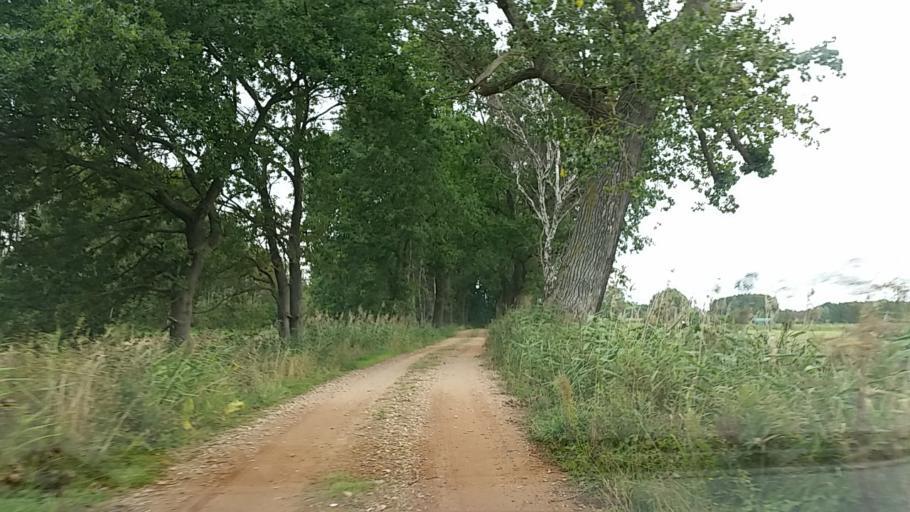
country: DE
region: Lower Saxony
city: Wieren
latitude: 52.9007
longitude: 10.6671
